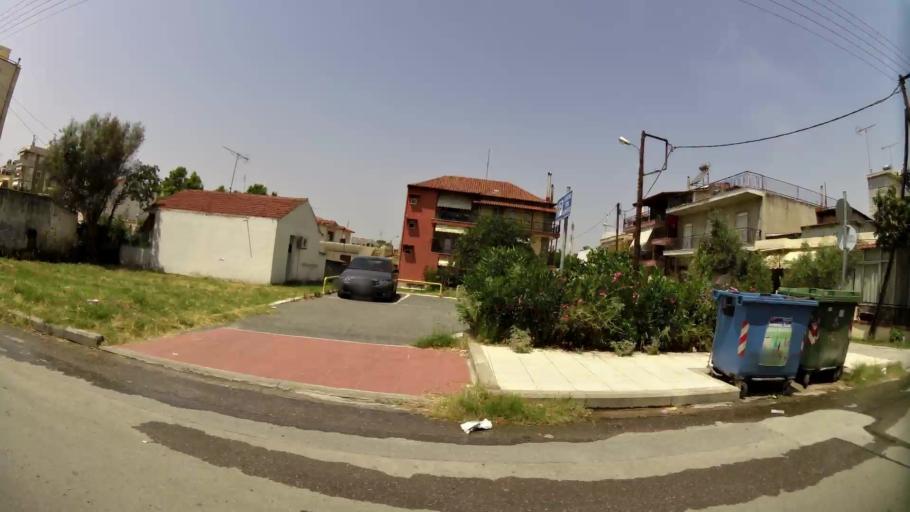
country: GR
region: Central Macedonia
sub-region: Nomos Thessalonikis
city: Menemeni
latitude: 40.6732
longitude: 22.8921
